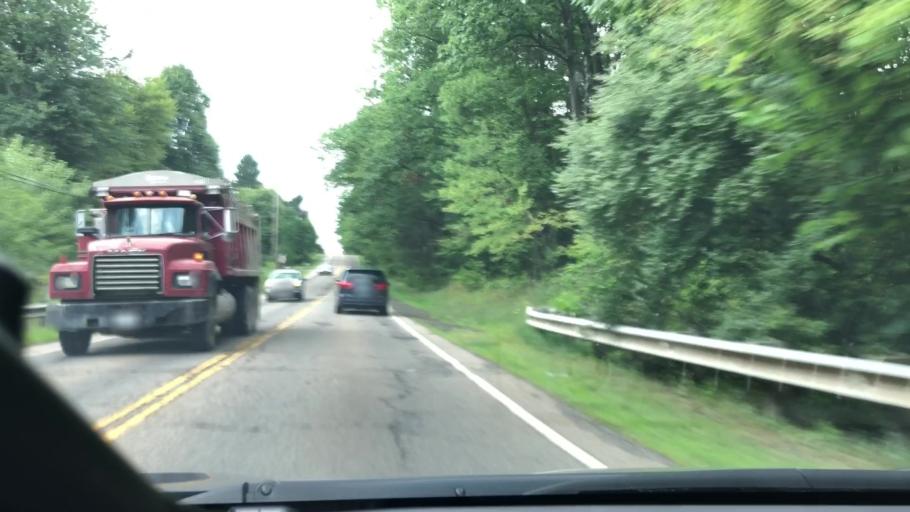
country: US
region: Ohio
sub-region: Summit County
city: New Franklin
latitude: 40.9347
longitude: -81.5348
